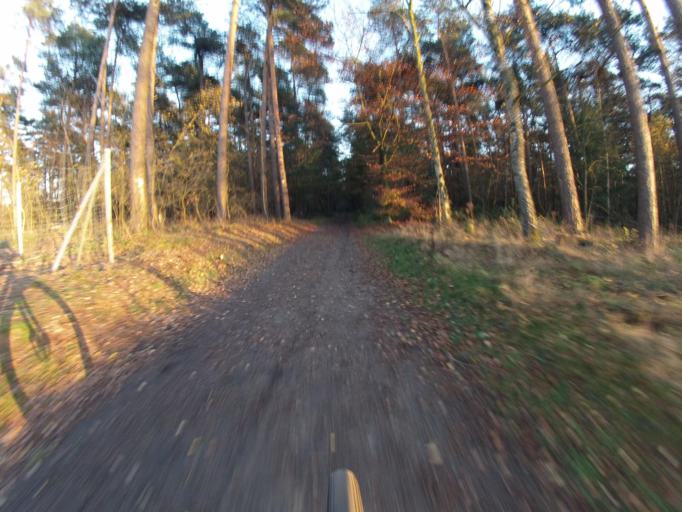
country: DE
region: North Rhine-Westphalia
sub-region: Regierungsbezirk Munster
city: Birgte
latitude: 52.2658
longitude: 7.6513
